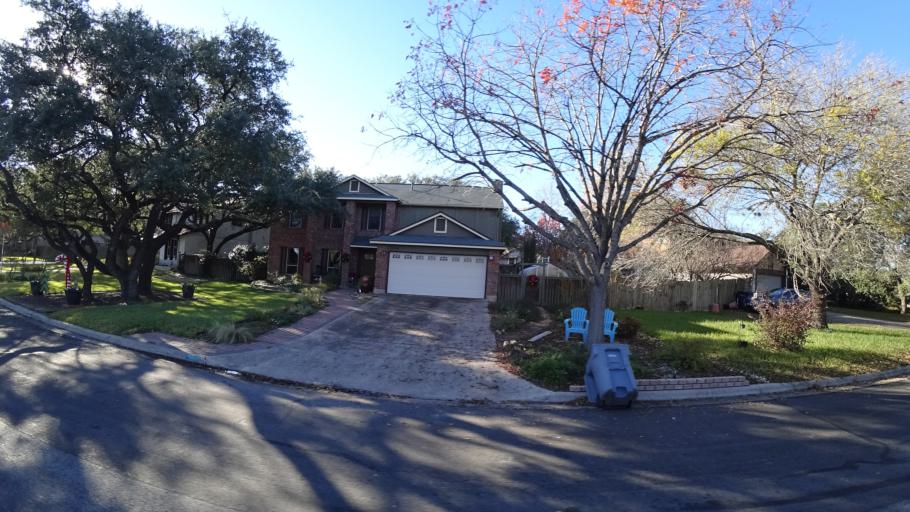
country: US
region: Texas
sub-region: Travis County
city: Wells Branch
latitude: 30.3995
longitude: -97.6922
